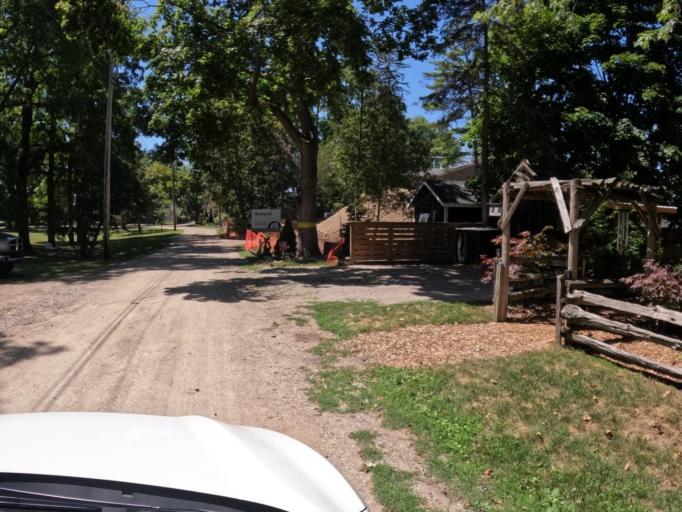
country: CA
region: Ontario
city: Cambridge
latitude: 43.4134
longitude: -80.2663
